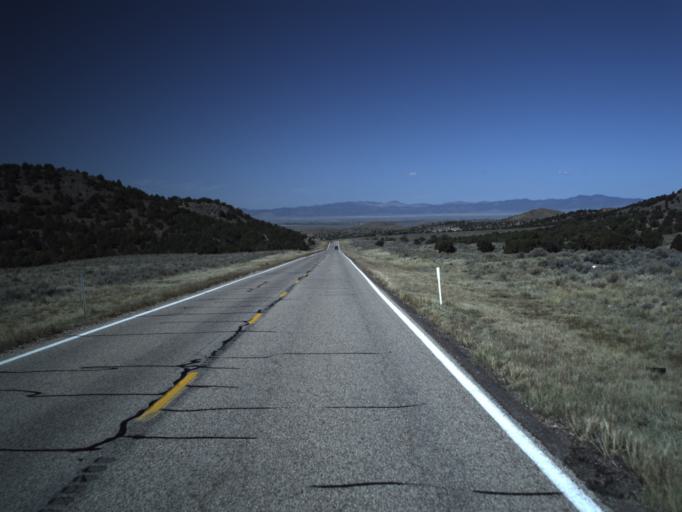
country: US
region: Utah
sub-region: Washington County
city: Enterprise
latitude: 37.6707
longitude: -113.4849
